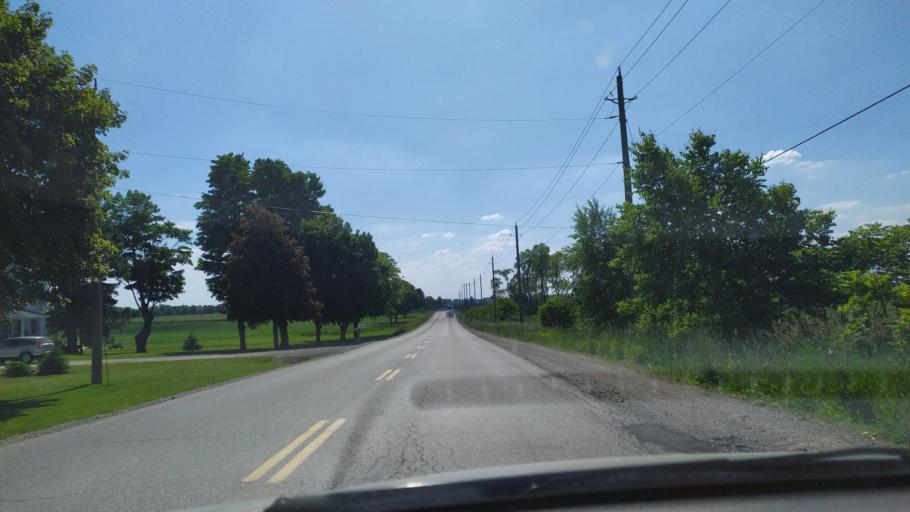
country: CA
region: Ontario
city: Kitchener
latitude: 43.3760
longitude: -80.5256
